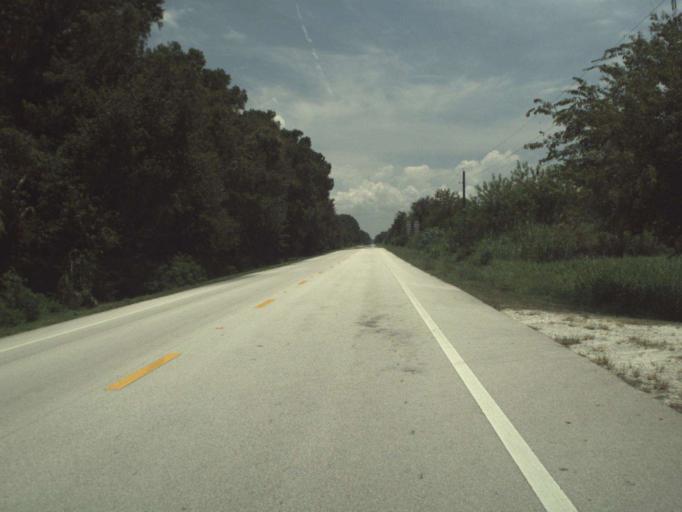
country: US
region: Florida
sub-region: Martin County
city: Indiantown
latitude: 27.0442
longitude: -80.6401
